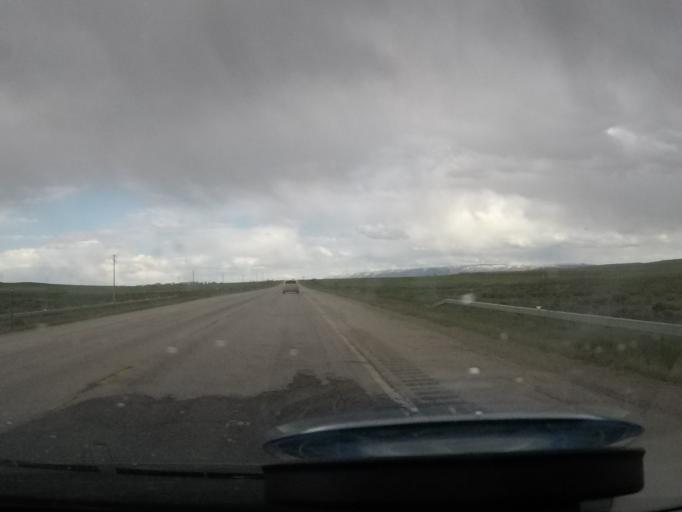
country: US
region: Wyoming
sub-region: Natrona County
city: Mills
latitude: 42.9587
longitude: -106.6555
